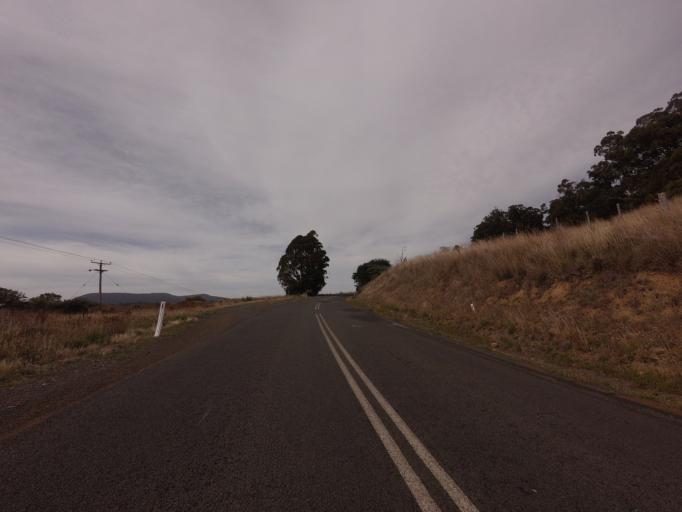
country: AU
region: Tasmania
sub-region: Sorell
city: Sorell
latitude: -42.4198
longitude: 147.4651
